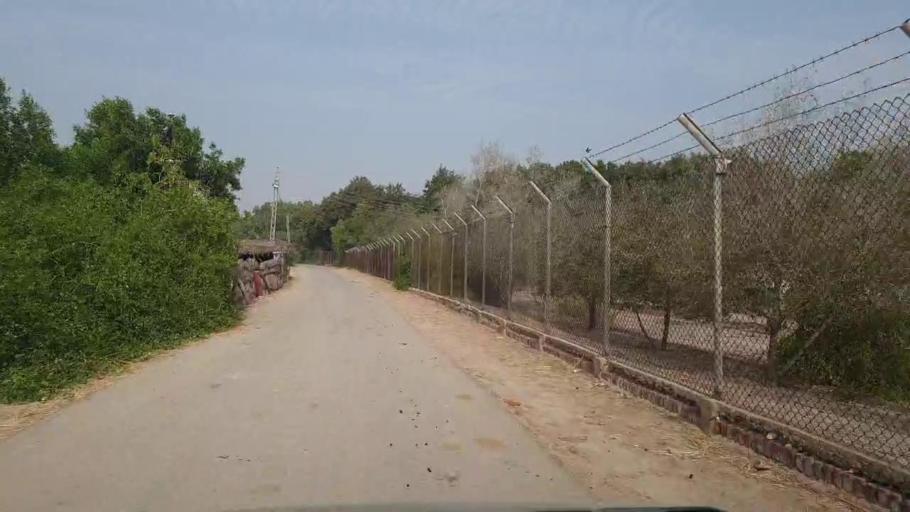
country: PK
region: Sindh
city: Tando Muhammad Khan
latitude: 25.1286
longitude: 68.4530
